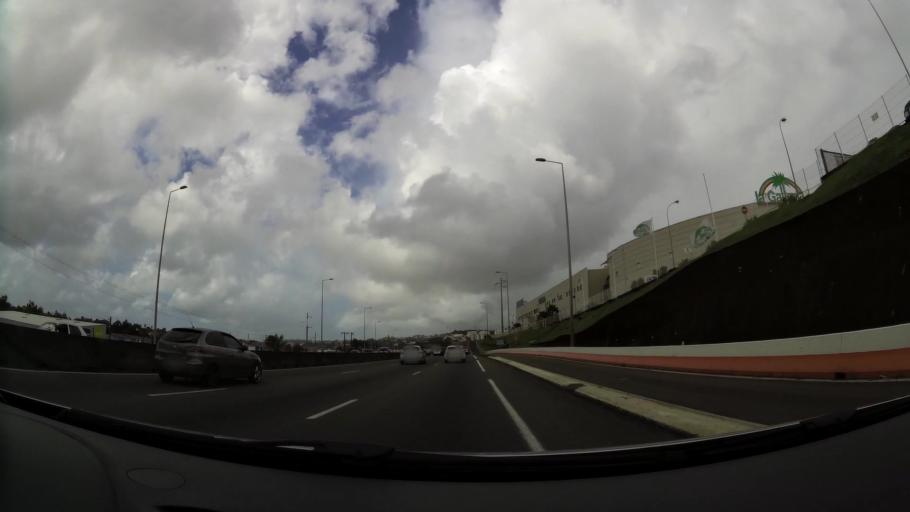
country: MQ
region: Martinique
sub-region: Martinique
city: Le Lamentin
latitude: 14.6179
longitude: -61.0187
